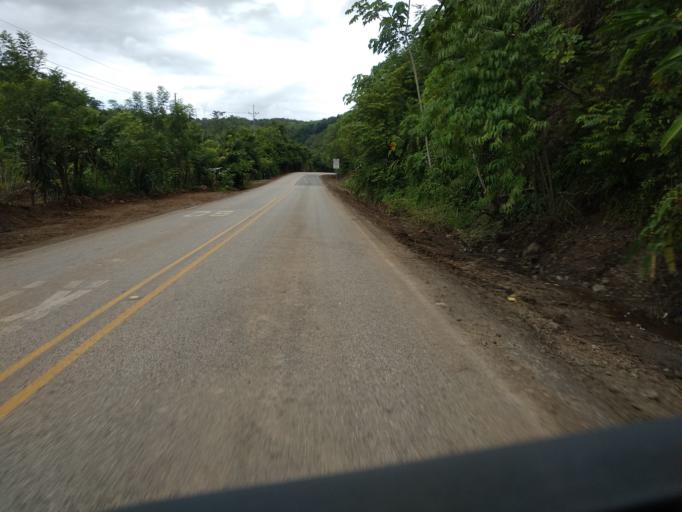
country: CR
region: Puntarenas
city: Buenos Aires
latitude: 9.0864
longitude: -83.2781
